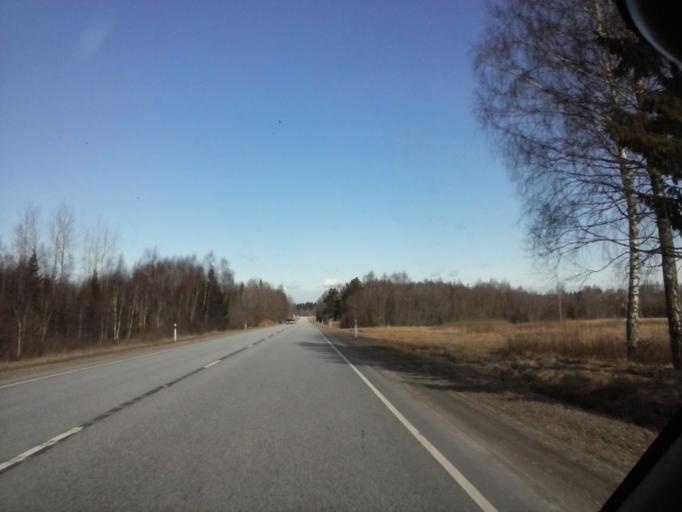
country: EE
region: Harju
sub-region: Anija vald
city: Kehra
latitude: 59.1563
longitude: 25.2910
